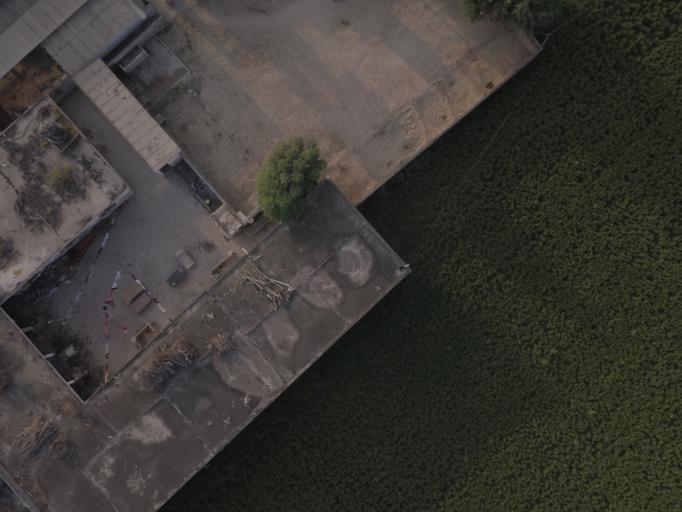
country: IN
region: Punjab
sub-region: Shahid Bhagat Singh Nagar
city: Rahon
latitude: 31.0174
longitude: 76.0889
